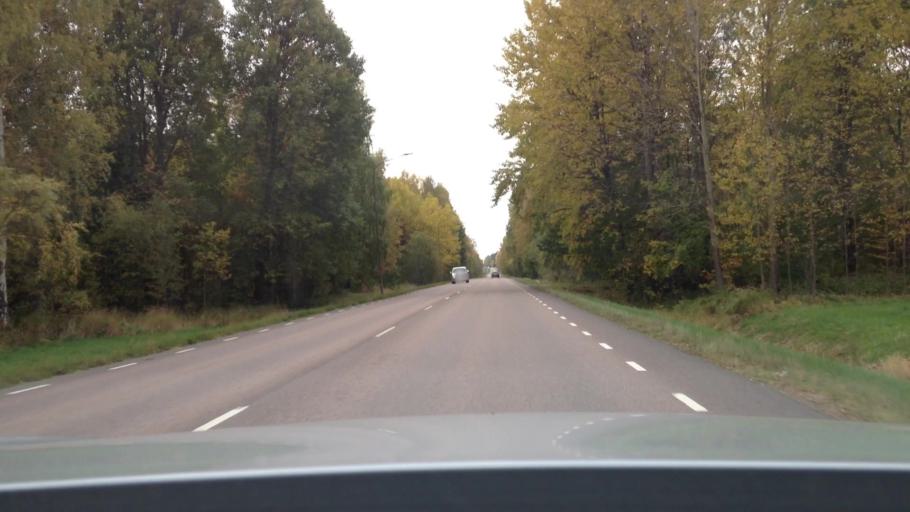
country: SE
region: Vaermland
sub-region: Karlstads Kommun
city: Karlstad
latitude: 59.3766
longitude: 13.4652
